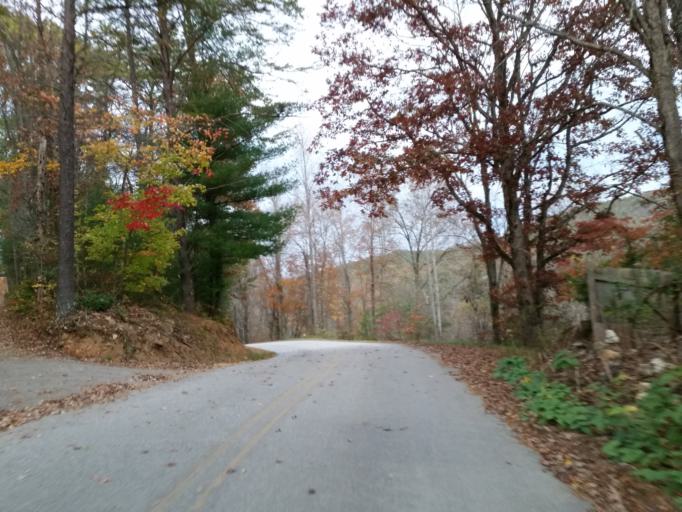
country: US
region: Georgia
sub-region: Fannin County
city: Blue Ridge
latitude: 34.7314
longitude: -84.1973
